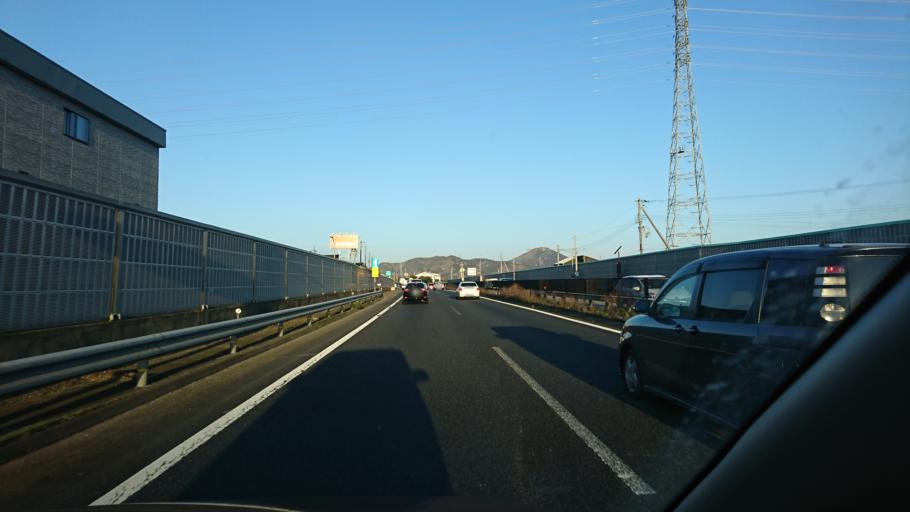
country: JP
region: Hyogo
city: Kakogawacho-honmachi
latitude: 34.7841
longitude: 134.8283
